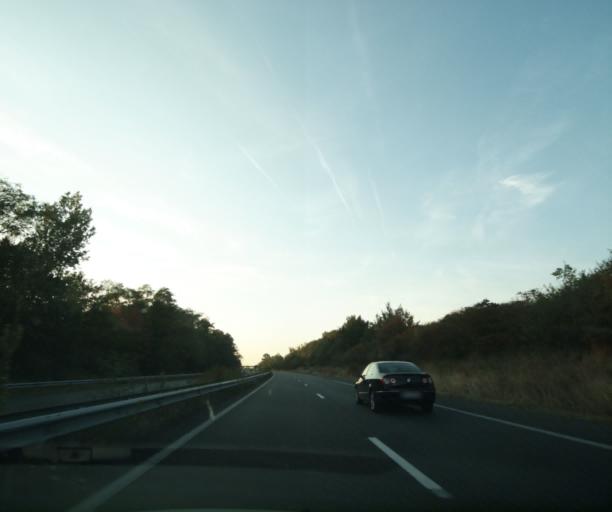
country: FR
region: Aquitaine
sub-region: Departement du Lot-et-Garonne
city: Buzet-sur-Baise
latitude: 44.2372
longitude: 0.3234
